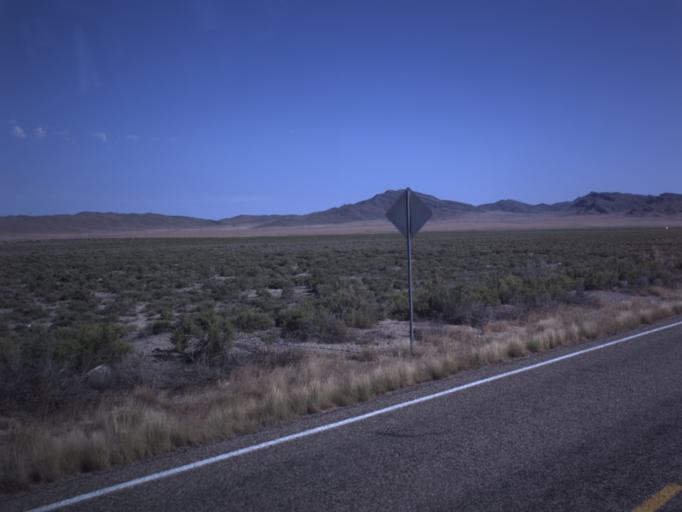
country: US
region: Utah
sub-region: Beaver County
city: Milford
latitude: 38.6931
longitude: -112.9746
